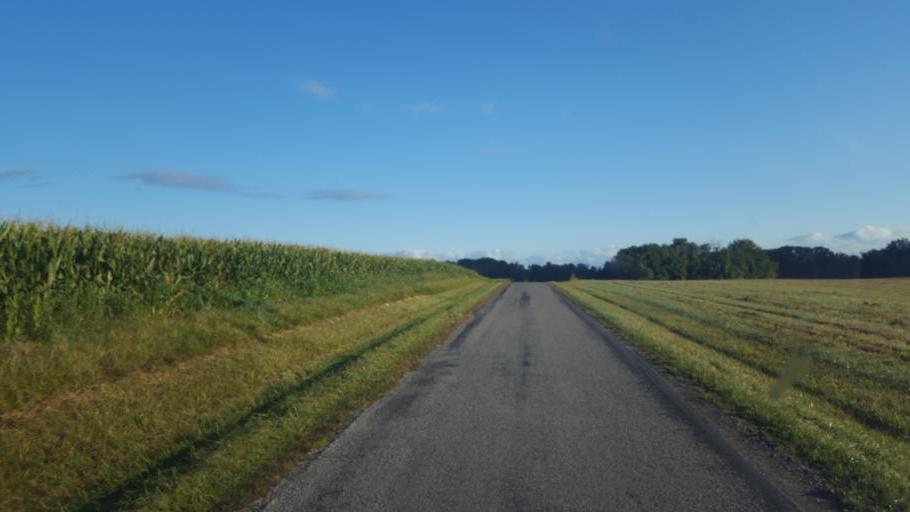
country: US
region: Ohio
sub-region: Lorain County
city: Wellington
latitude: 41.0771
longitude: -82.2795
